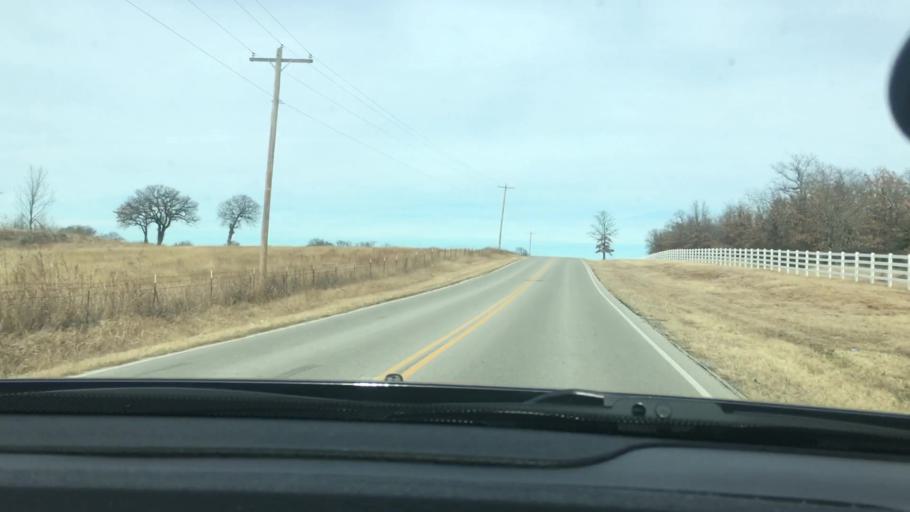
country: US
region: Oklahoma
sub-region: Carter County
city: Ardmore
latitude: 34.1818
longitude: -97.0731
